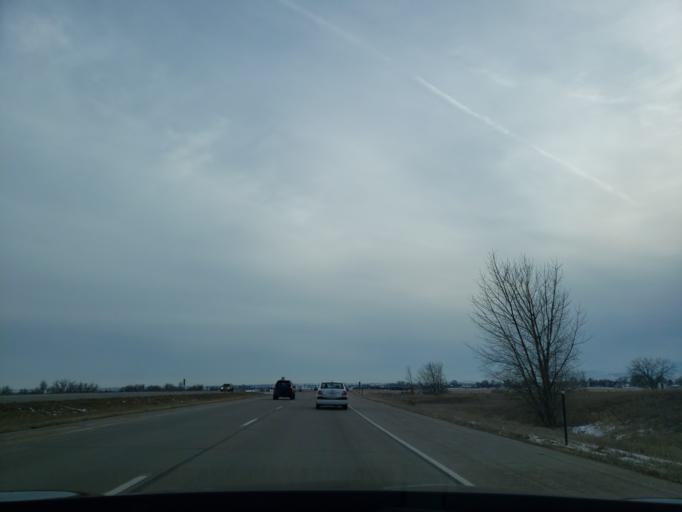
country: US
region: Colorado
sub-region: Larimer County
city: Berthoud
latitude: 40.3233
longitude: -105.1025
